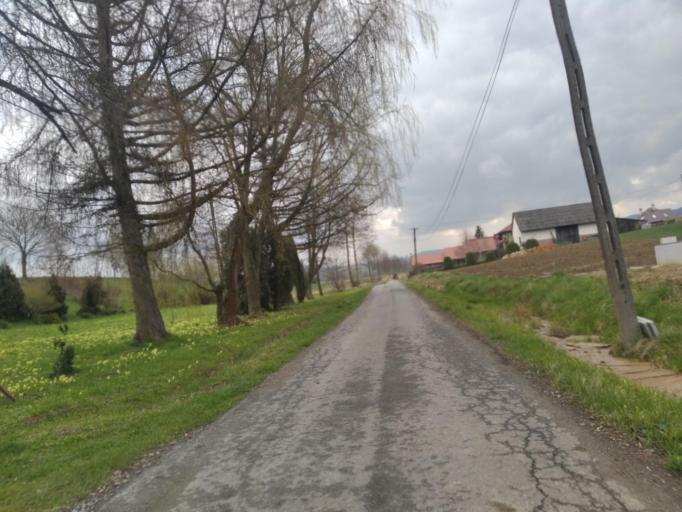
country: PL
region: Subcarpathian Voivodeship
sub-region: Powiat strzyzowski
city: Wisniowa
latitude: 49.8789
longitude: 21.7056
